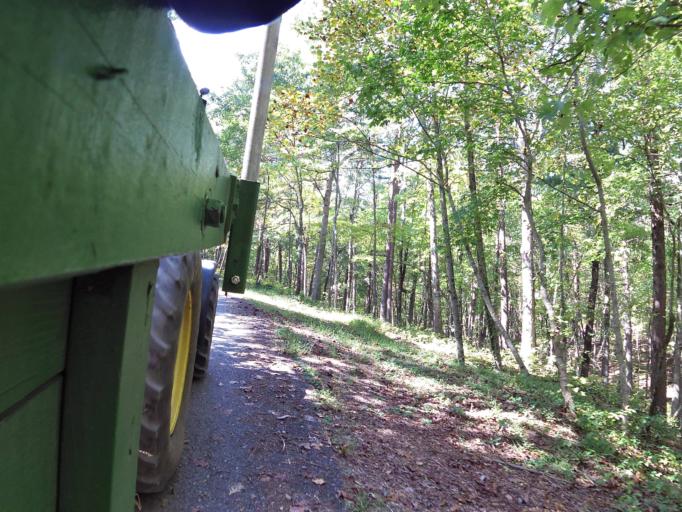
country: US
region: Georgia
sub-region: Dawson County
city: Dawsonville
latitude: 34.5437
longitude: -84.2515
